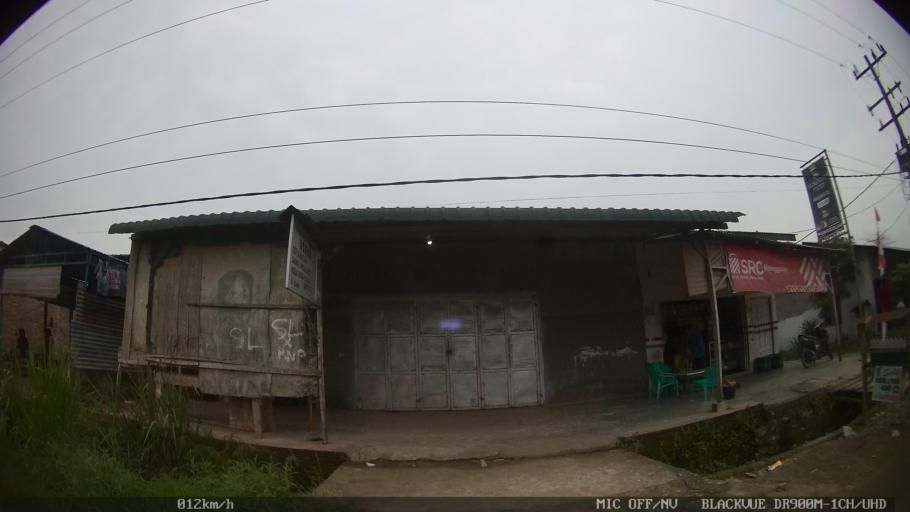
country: ID
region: North Sumatra
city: Deli Tua
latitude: 3.5456
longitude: 98.7277
